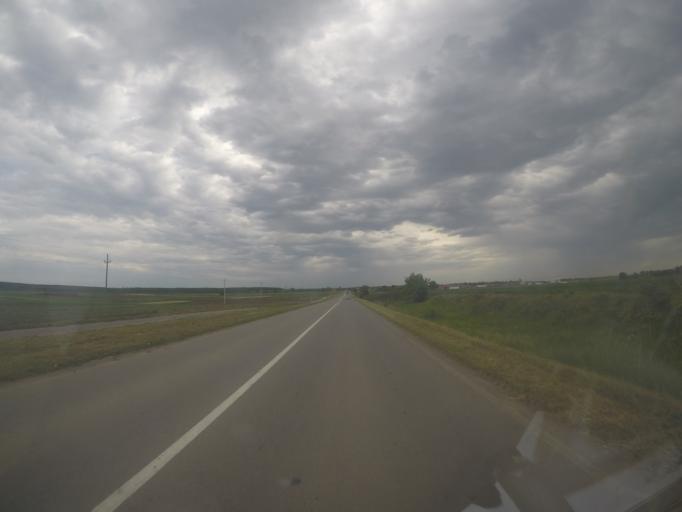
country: RS
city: Baranda
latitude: 45.0706
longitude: 20.4380
